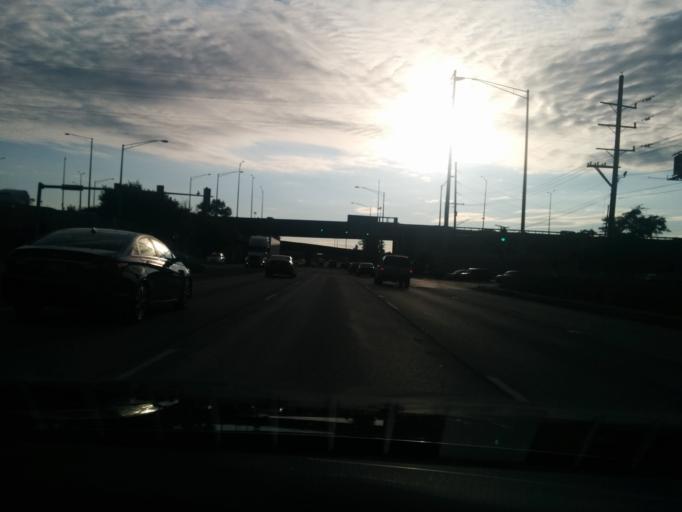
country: US
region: Illinois
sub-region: Cook County
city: Berkeley
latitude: 41.9069
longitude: -87.9174
